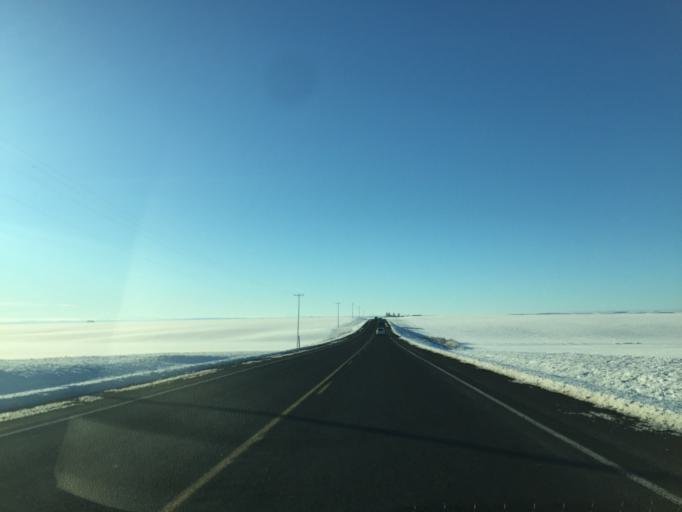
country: US
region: Washington
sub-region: Okanogan County
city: Coulee Dam
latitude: 47.6845
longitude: -118.9987
